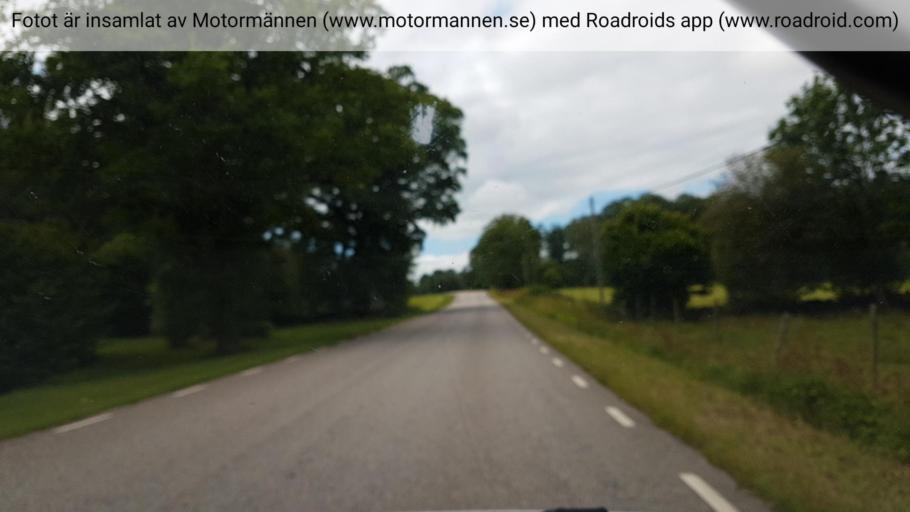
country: SE
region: Vaestra Goetaland
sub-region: Ulricehamns Kommun
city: Ulricehamn
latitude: 57.8014
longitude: 13.5776
